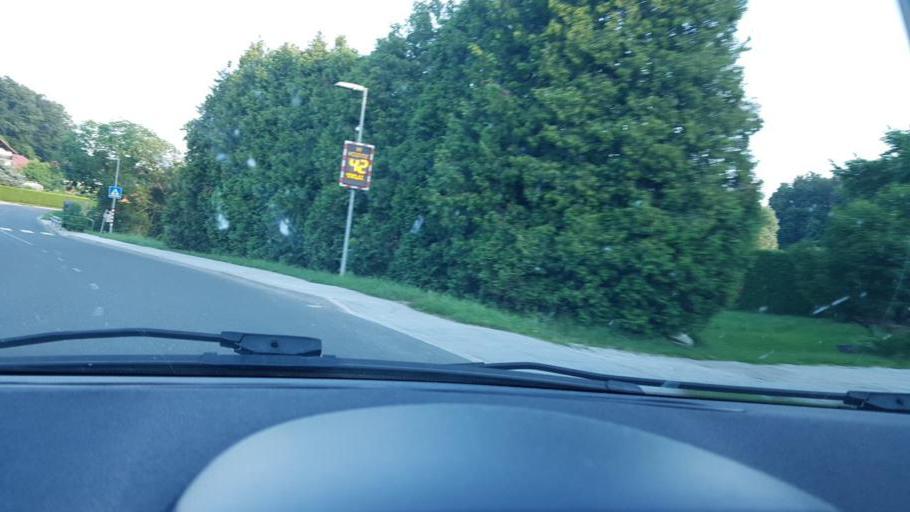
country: SI
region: Rogaska Slatina
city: Rogaska Slatina
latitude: 46.2513
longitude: 15.6211
